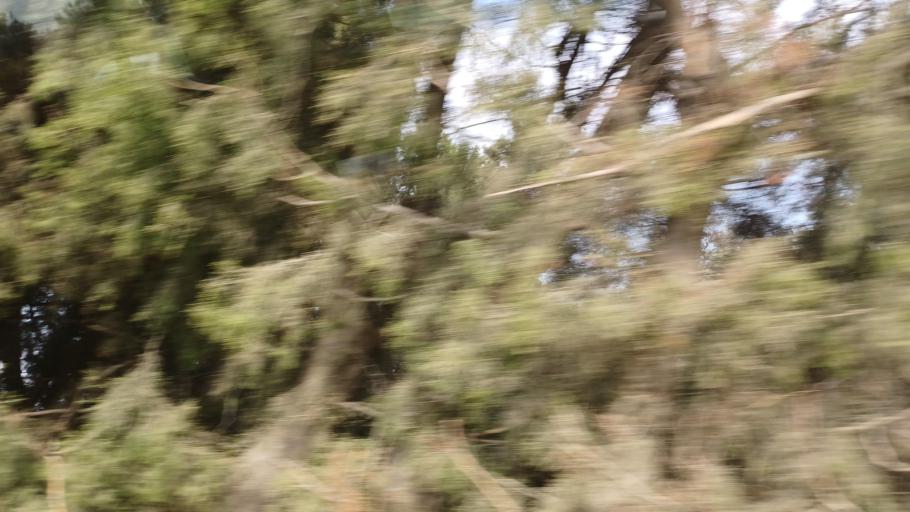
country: CY
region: Larnaka
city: Kolossi
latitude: 34.6659
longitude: 32.9391
